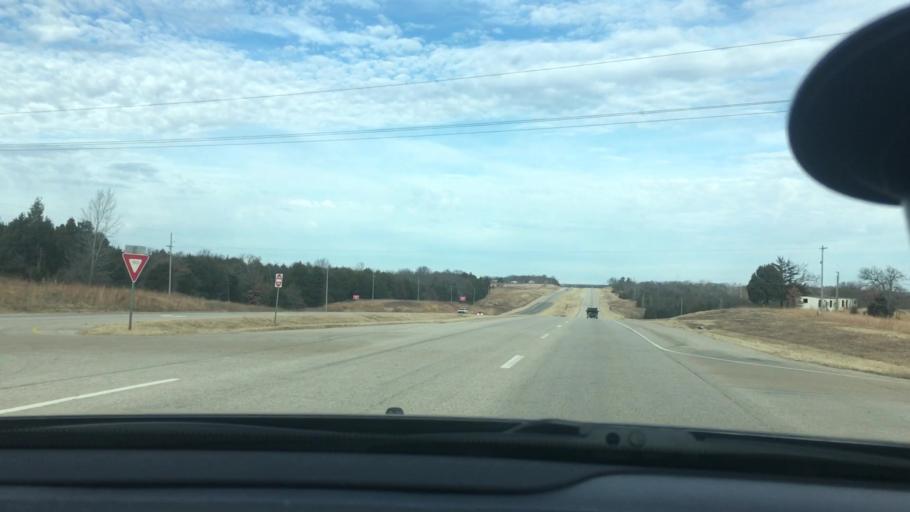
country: US
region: Oklahoma
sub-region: Pontotoc County
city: Byng
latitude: 34.9047
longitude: -96.6762
